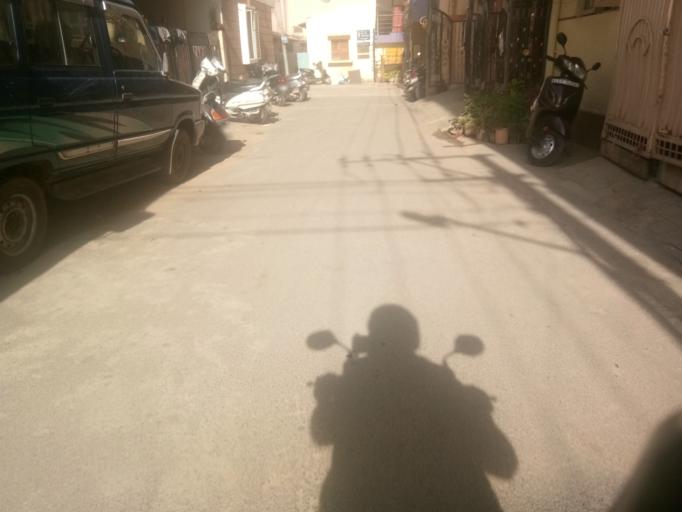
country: IN
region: Karnataka
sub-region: Bangalore Urban
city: Bangalore
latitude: 13.0060
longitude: 77.6012
